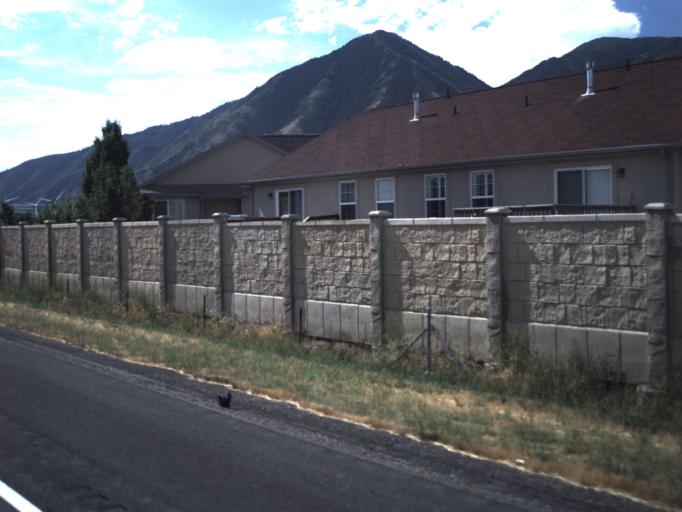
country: US
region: Utah
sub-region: Utah County
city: Mapleton
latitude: 40.0932
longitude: -111.6011
